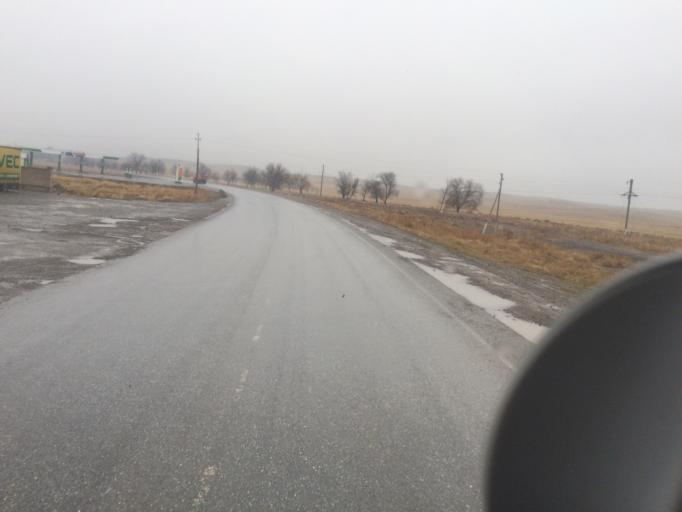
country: KG
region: Chuy
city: Kant
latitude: 43.0042
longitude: 74.8623
